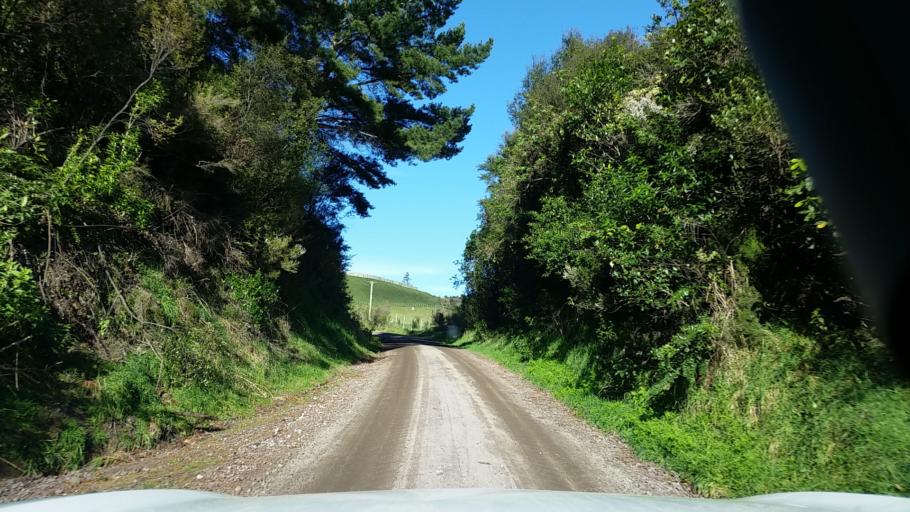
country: NZ
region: Waikato
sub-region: Taupo District
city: Taupo
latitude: -38.4051
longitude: 176.1399
